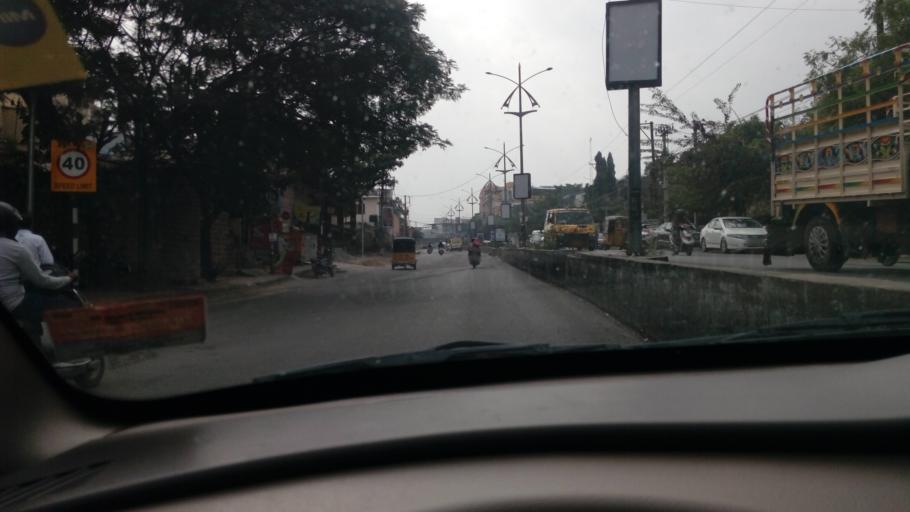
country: IN
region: Telangana
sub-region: Rangareddi
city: Kukatpalli
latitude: 17.4343
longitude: 78.4087
